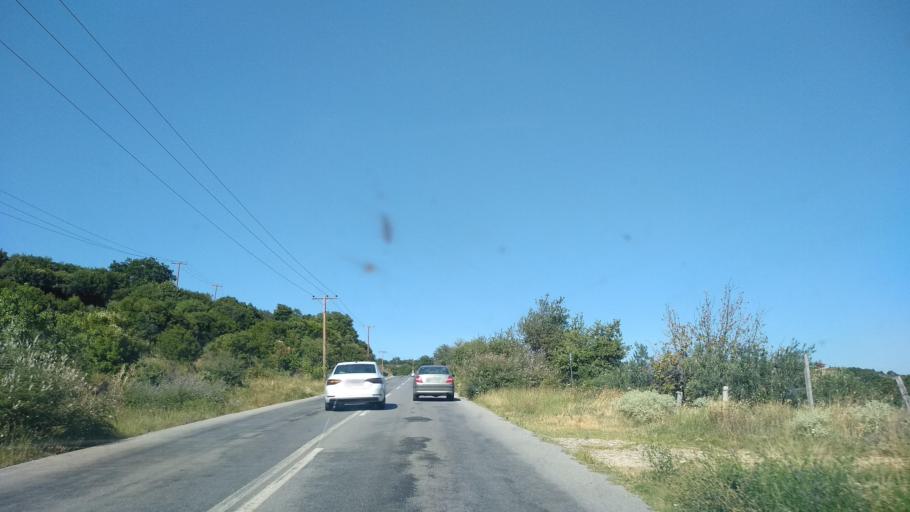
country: GR
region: Central Macedonia
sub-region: Nomos Chalkidikis
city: Megali Panagia
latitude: 40.3922
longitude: 23.6852
